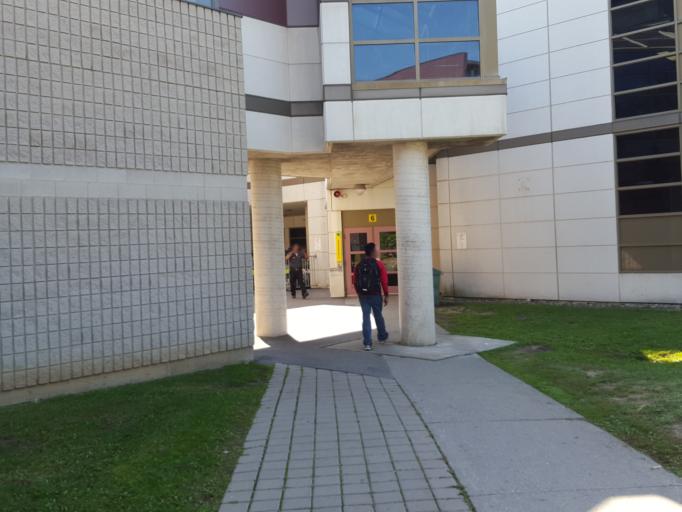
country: CA
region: Ontario
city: Scarborough
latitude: 43.7848
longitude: -79.2284
